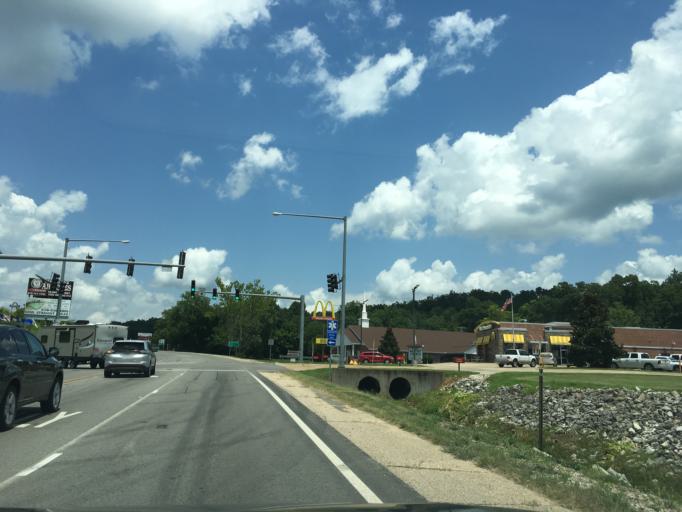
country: US
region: Arkansas
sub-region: Sharp County
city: Cherokee Village
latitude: 36.3171
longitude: -91.4871
